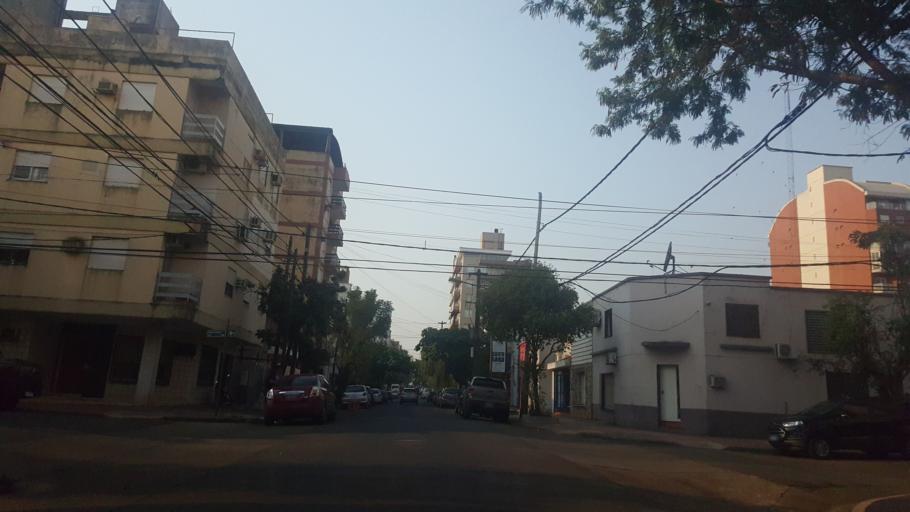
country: AR
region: Misiones
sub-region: Departamento de Capital
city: Posadas
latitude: -27.3713
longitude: -55.8910
